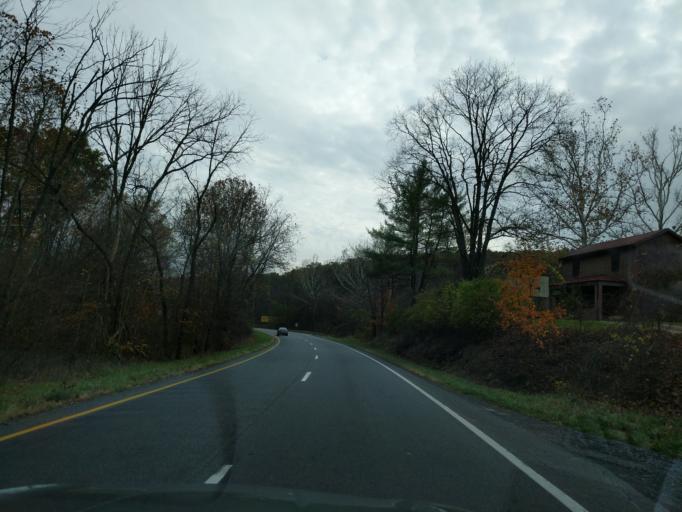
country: US
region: Virginia
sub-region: Frederick County
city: Shawnee Land
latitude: 39.3363
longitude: -78.3081
